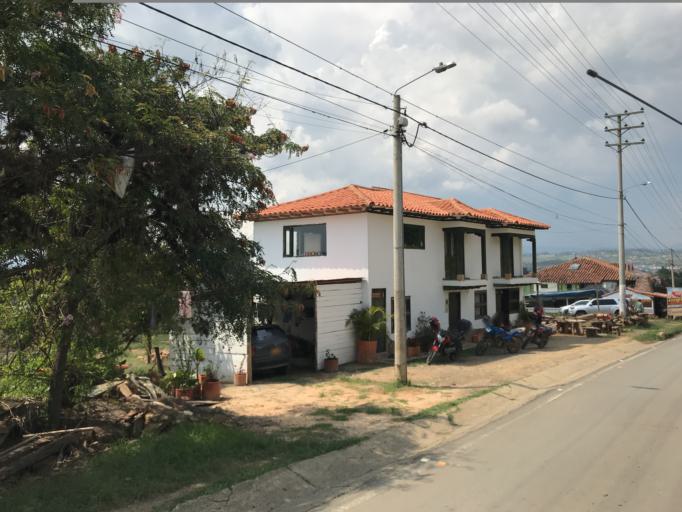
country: CO
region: Boyaca
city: Sachica
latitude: 5.6236
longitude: -73.5314
